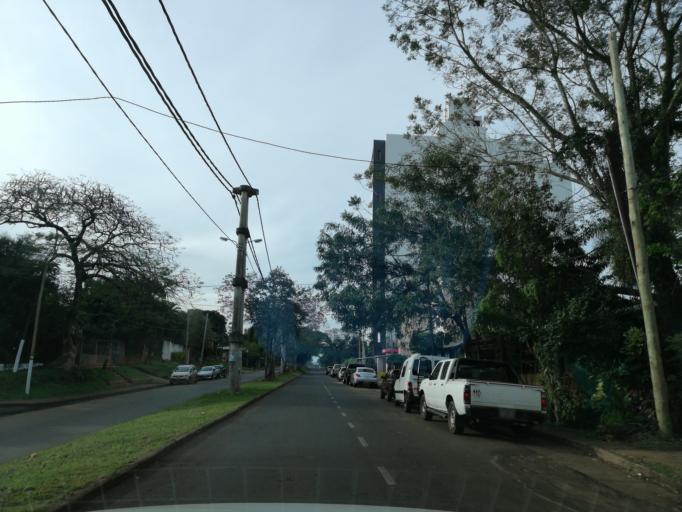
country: AR
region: Misiones
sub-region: Departamento de Capital
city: Posadas
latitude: -27.3620
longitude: -55.9120
